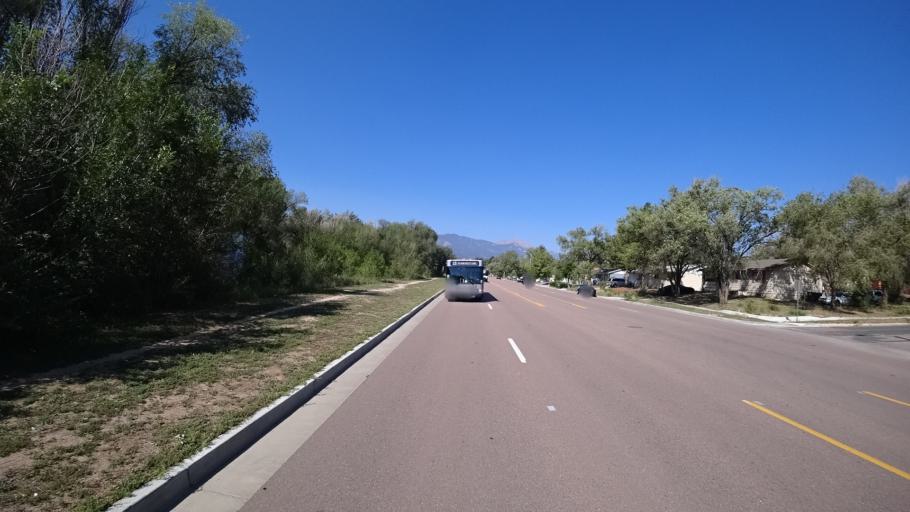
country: US
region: Colorado
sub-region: El Paso County
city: Colorado Springs
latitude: 38.8173
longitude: -104.7863
